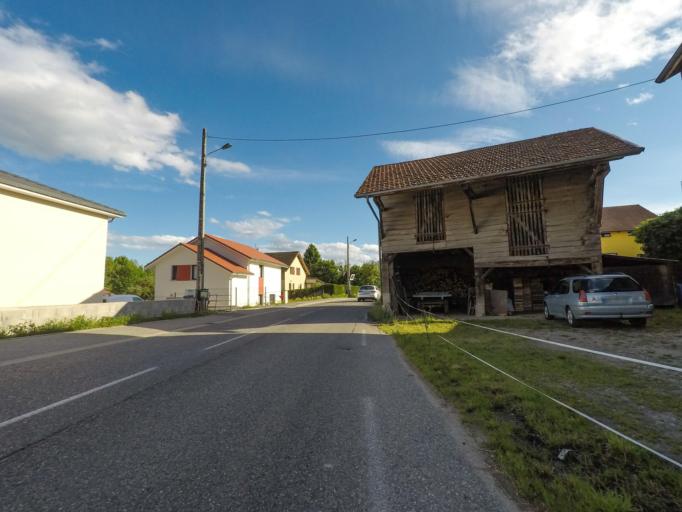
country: FR
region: Rhone-Alpes
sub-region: Departement de l'Ain
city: Saint-Genis-Pouilly
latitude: 46.2538
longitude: 6.0351
